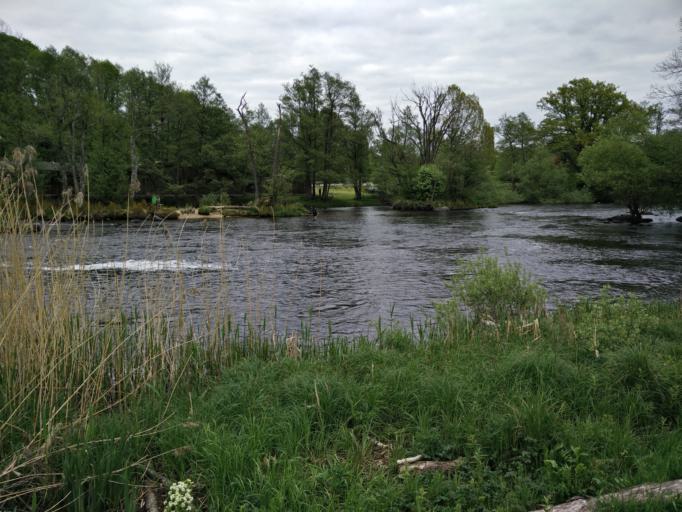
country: SE
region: Blekinge
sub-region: Karlshamns Kommun
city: Morrum
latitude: 56.1916
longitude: 14.7492
